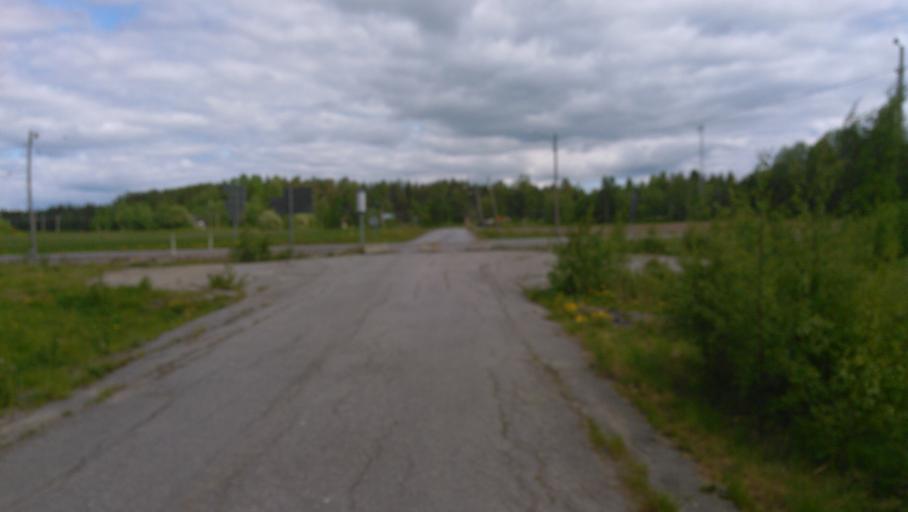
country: SE
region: Vaesterbotten
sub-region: Umea Kommun
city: Roback
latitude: 63.8780
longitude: 20.0533
